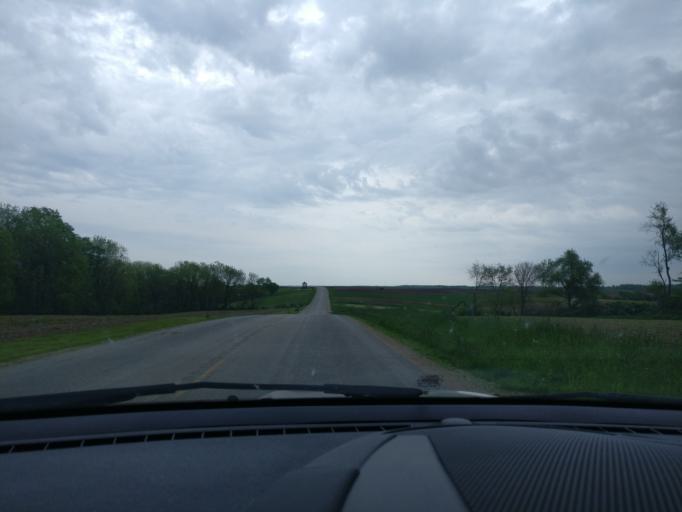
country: US
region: Wisconsin
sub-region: Lafayette County
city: Darlington
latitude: 42.7485
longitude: -89.9835
